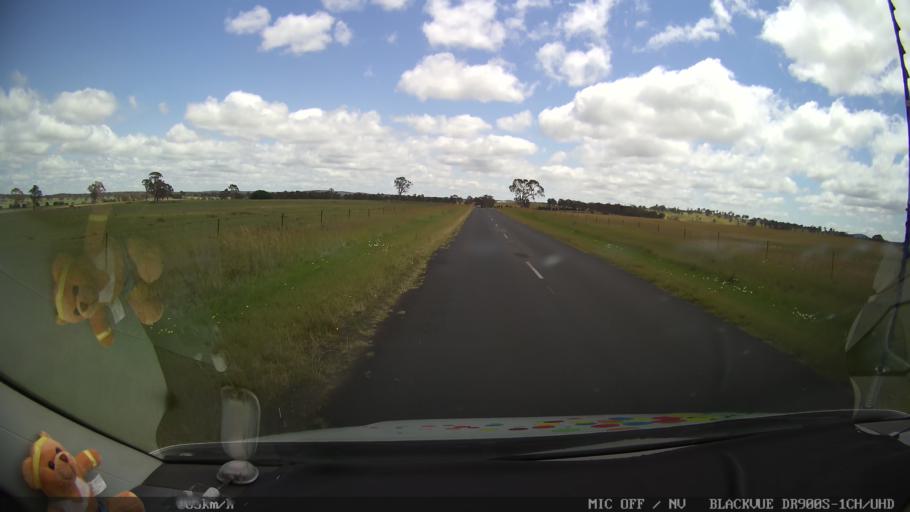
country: AU
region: New South Wales
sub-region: Glen Innes Severn
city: Glen Innes
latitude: -29.6588
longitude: 151.6926
